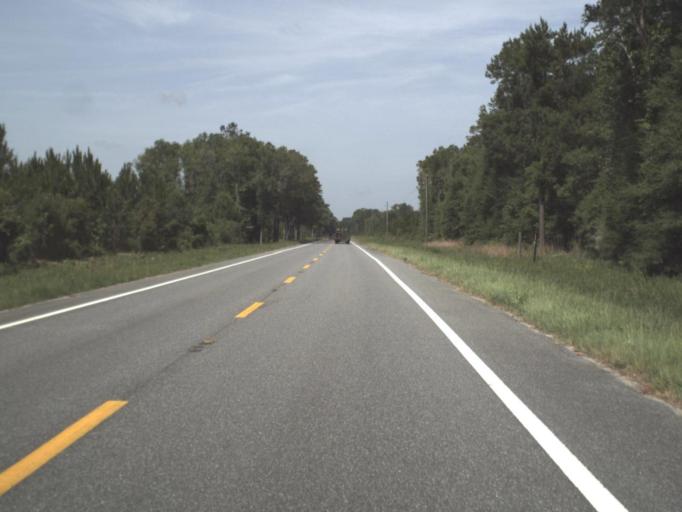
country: US
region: Florida
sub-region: Lafayette County
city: Mayo
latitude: 29.9577
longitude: -83.2455
